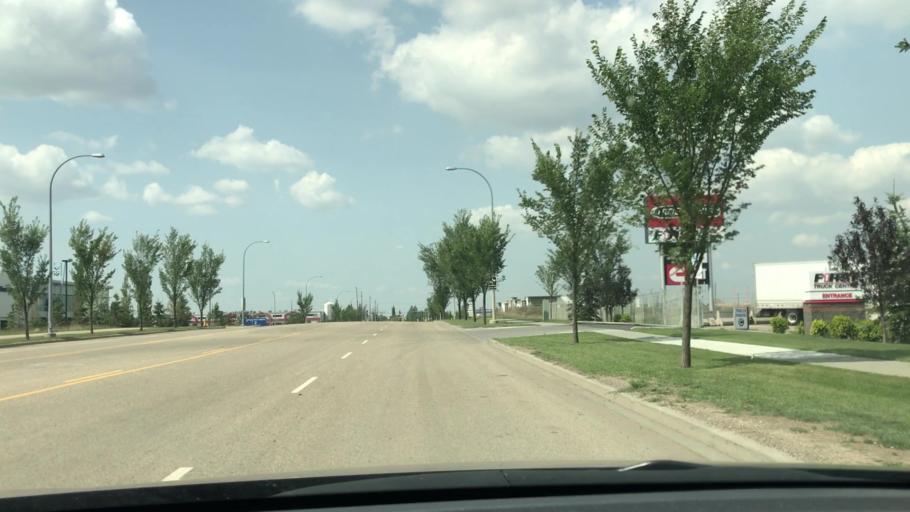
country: CA
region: Alberta
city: Edmonton
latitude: 53.4956
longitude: -113.4116
